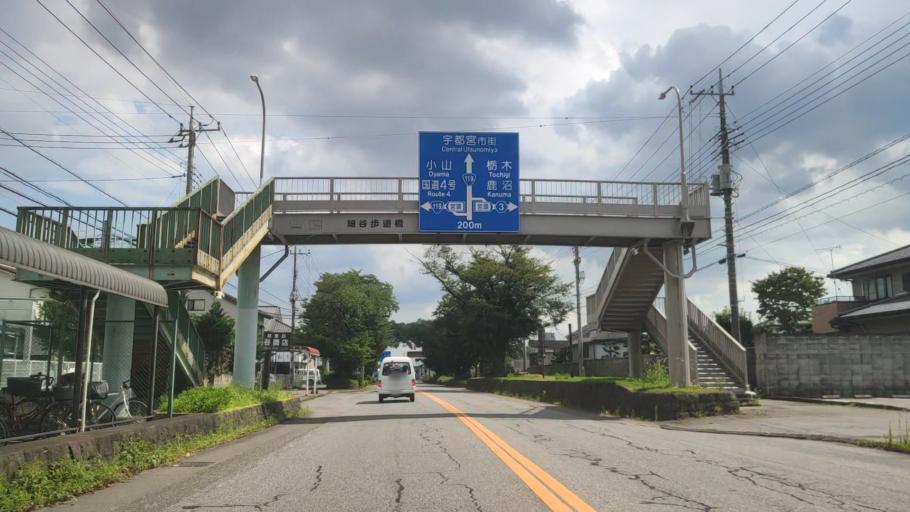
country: JP
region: Tochigi
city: Utsunomiya-shi
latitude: 36.5931
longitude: 139.8620
